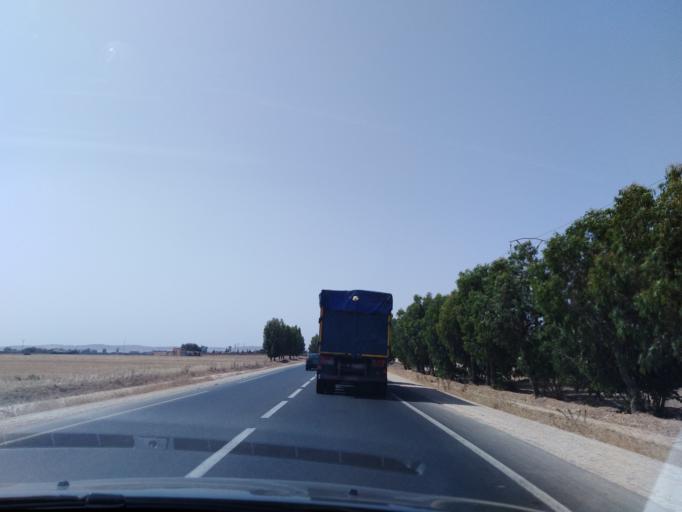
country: MA
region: Chaouia-Ouardigha
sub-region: Settat Province
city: Settat
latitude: 33.1341
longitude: -7.6255
